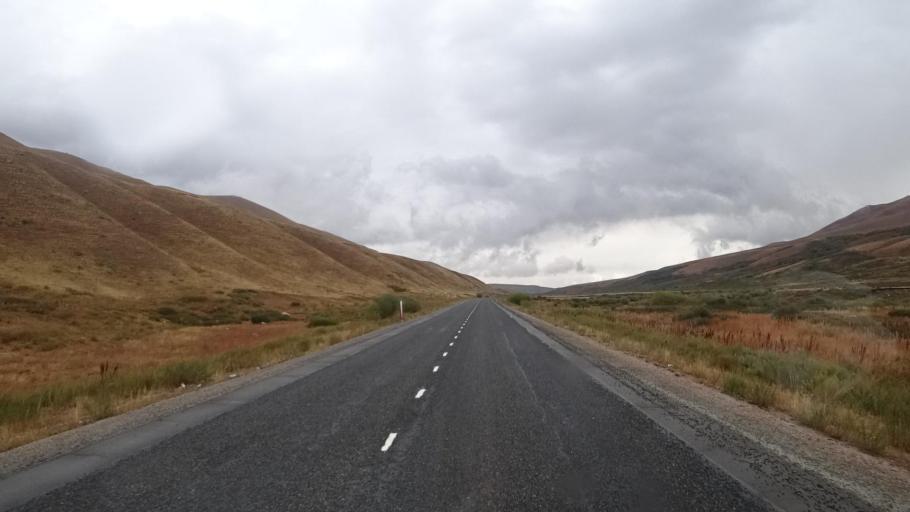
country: KG
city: Sosnovka
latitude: 42.2002
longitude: 73.5818
